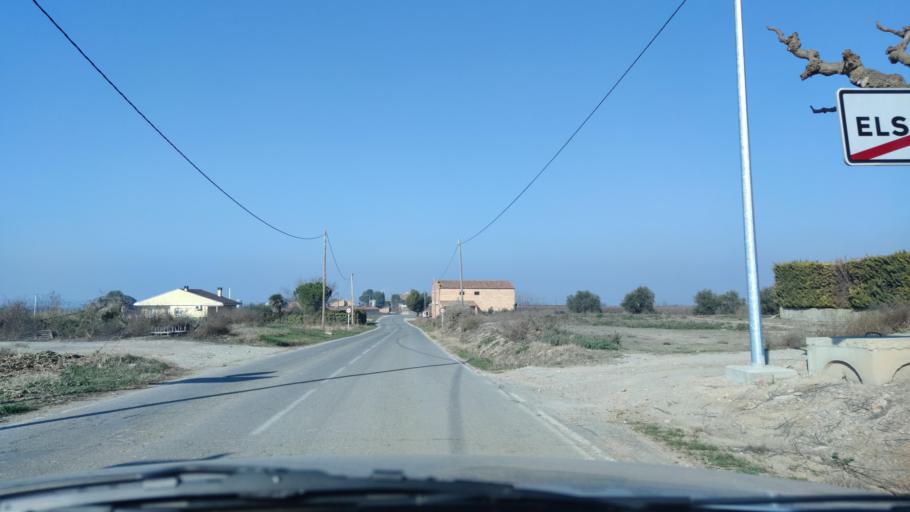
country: ES
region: Catalonia
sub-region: Provincia de Lleida
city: Alcoletge
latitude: 41.6170
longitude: 0.7357
